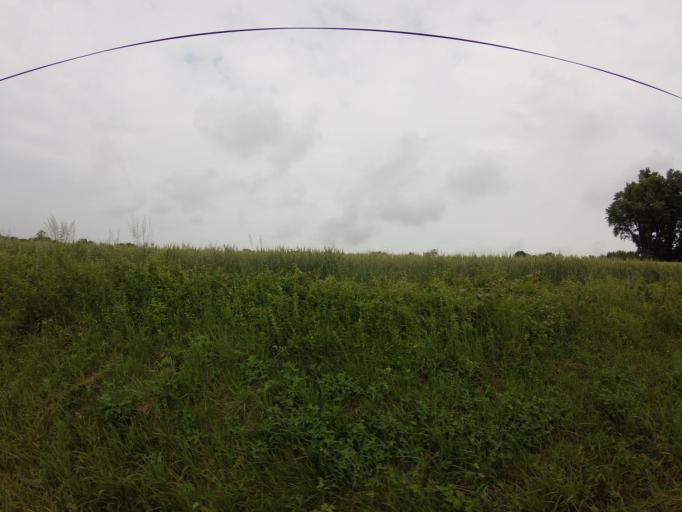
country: US
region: Maryland
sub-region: Frederick County
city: Jefferson
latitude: 39.3412
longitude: -77.5402
